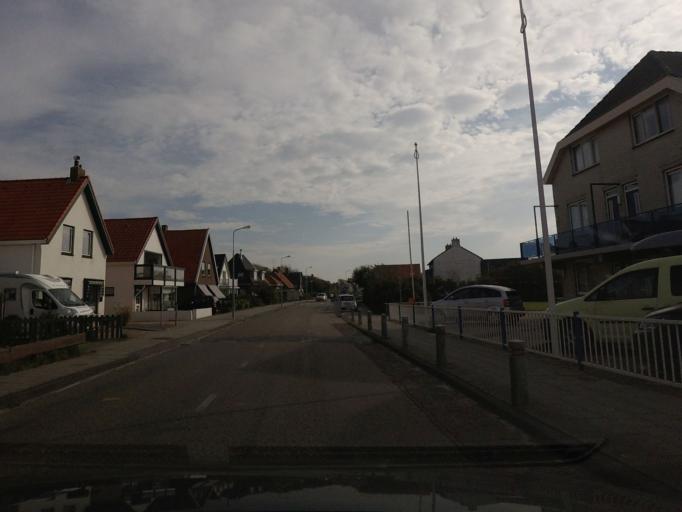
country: NL
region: North Holland
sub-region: Gemeente Schagen
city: Schagen
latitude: 52.8380
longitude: 4.6953
